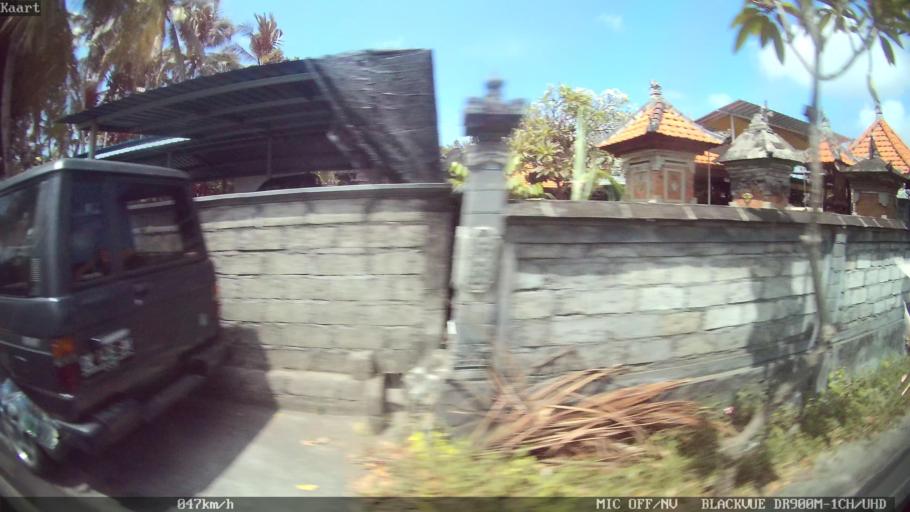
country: ID
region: Bali
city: Banjar Pasekan
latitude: -8.5996
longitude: 115.3016
